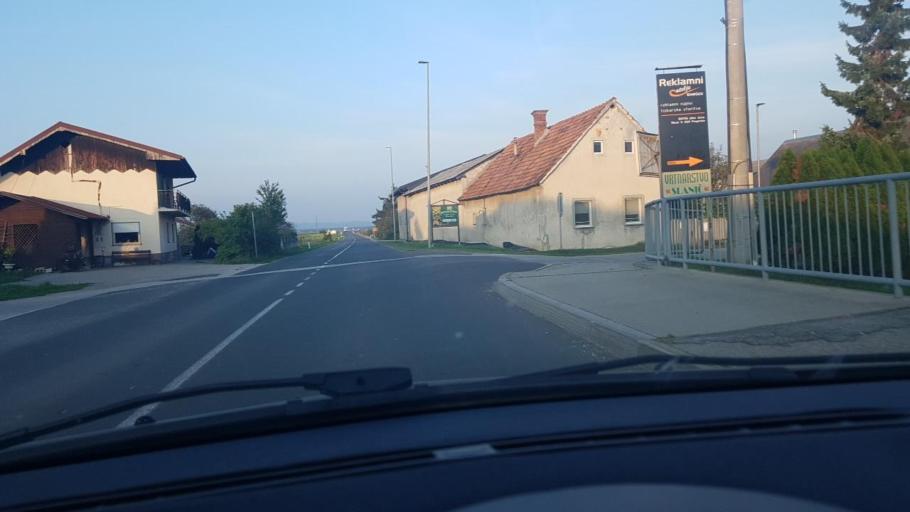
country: SI
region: Slovenska Bistrica
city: Pragersko
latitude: 46.4044
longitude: 15.7014
